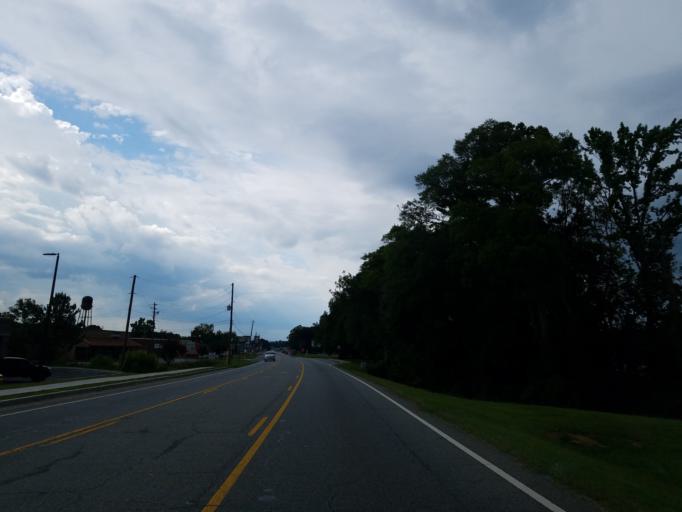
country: US
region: Georgia
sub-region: Bartow County
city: Adairsville
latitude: 34.3705
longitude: -84.9281
